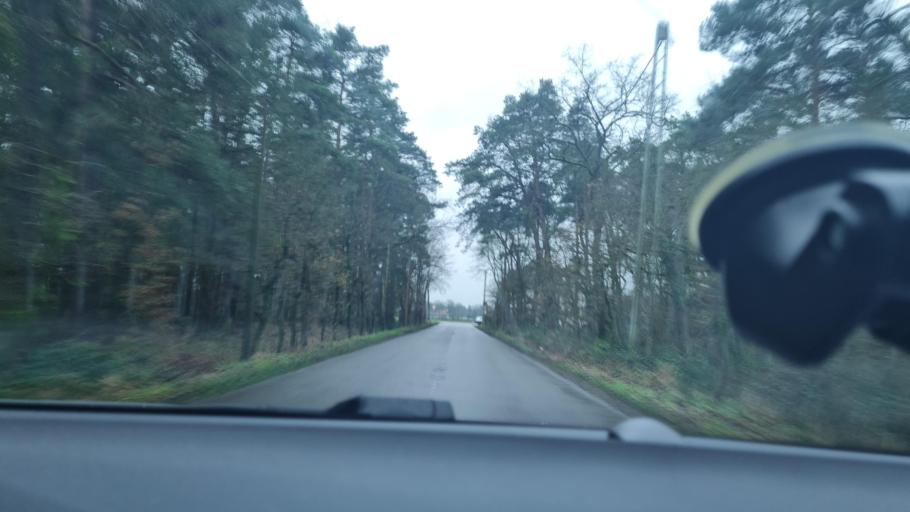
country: DE
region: North Rhine-Westphalia
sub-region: Regierungsbezirk Munster
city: Raesfeld
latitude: 51.7564
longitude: 6.8979
